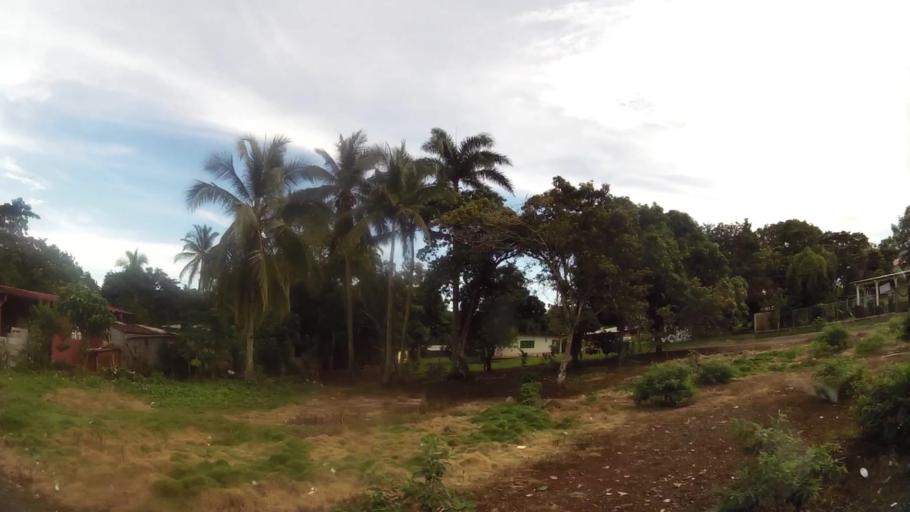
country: PA
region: Panama
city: El Coco
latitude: 8.8798
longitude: -79.8035
